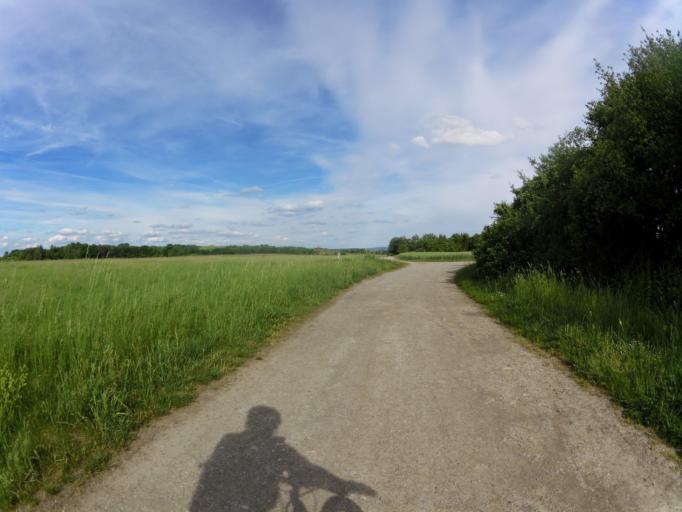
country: DE
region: Bavaria
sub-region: Regierungsbezirk Unterfranken
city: Ochsenfurt
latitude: 49.6735
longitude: 10.0696
